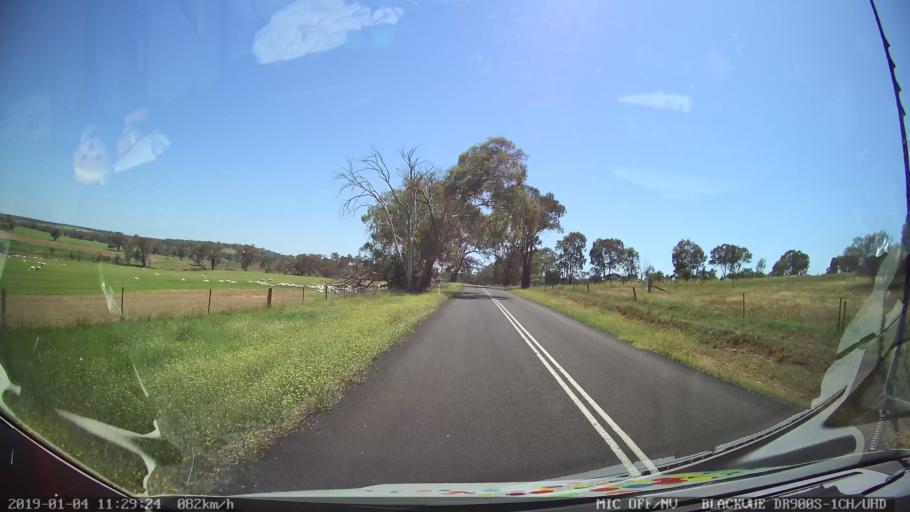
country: AU
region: New South Wales
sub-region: Cabonne
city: Molong
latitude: -33.0883
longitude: 148.7739
